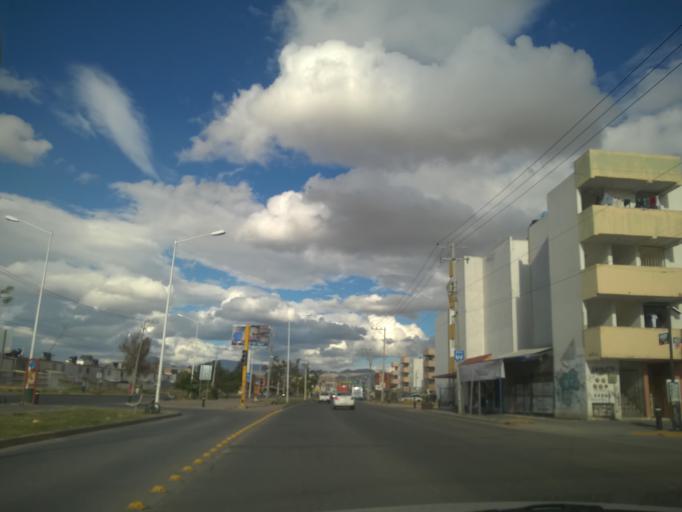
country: MX
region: Guanajuato
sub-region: Leon
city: San Jose de Duran (Los Troncoso)
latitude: 21.0799
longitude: -101.6324
